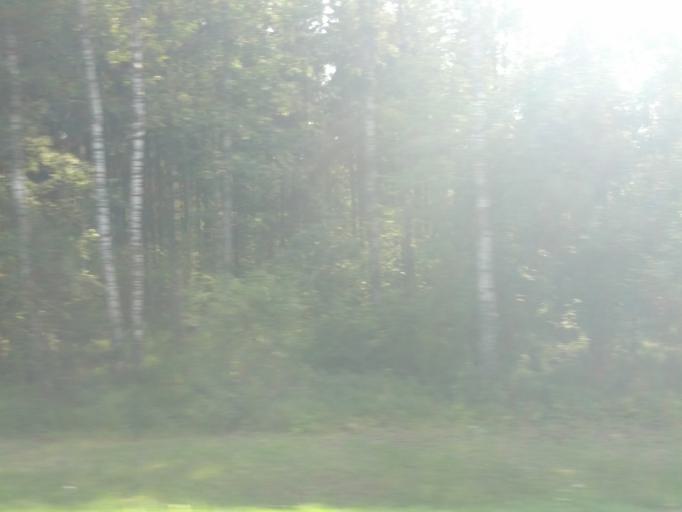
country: RU
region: Leningrad
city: Yanino Vtoroye
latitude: 59.8899
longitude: 30.5730
